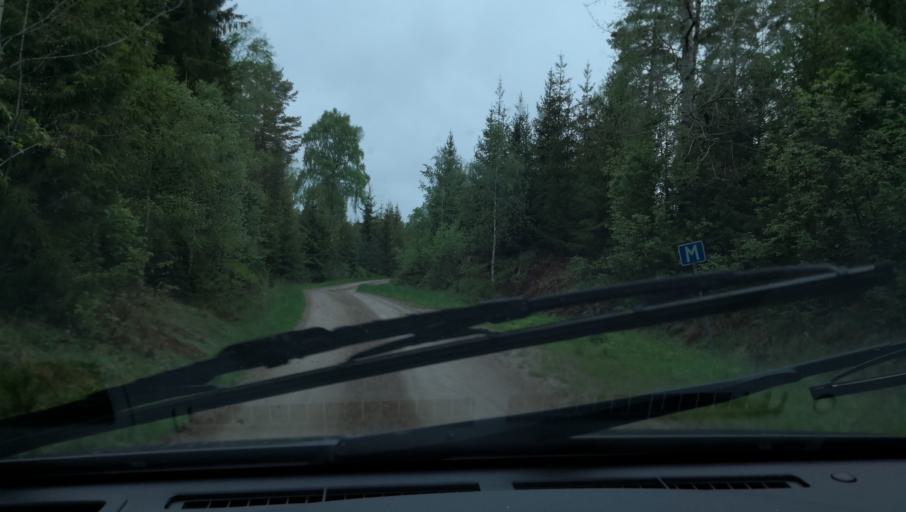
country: SE
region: Uppsala
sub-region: Enkopings Kommun
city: Orsundsbro
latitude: 59.9221
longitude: 17.3418
